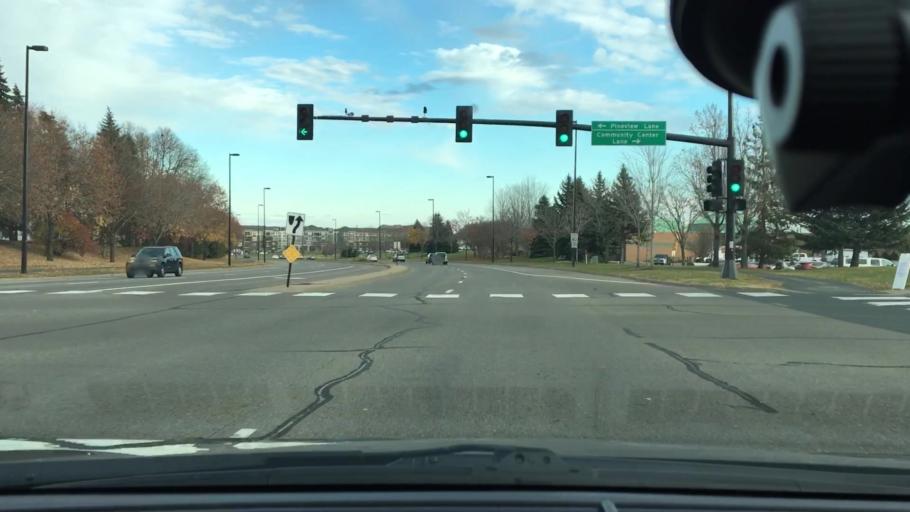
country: US
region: Minnesota
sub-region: Hennepin County
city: Maple Grove
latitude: 45.1042
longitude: -93.4447
